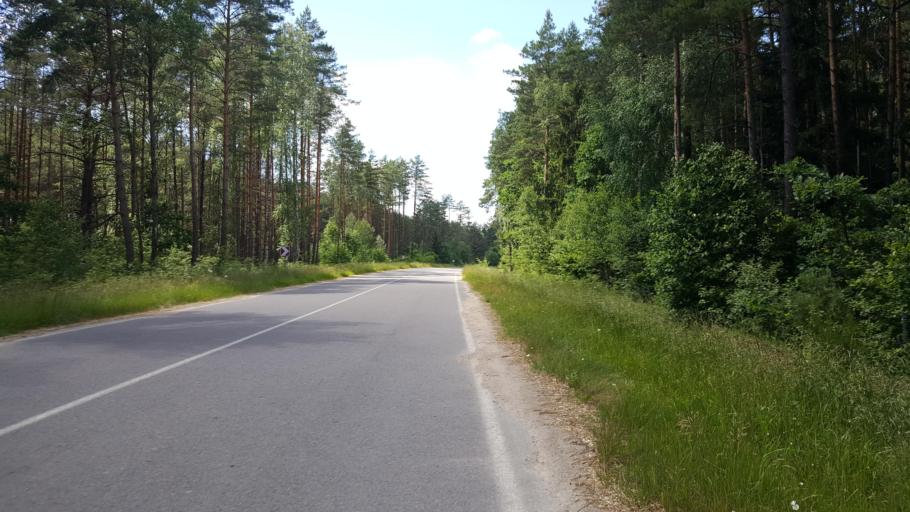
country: PL
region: Podlasie
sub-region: Powiat hajnowski
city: Czeremcha
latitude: 52.5436
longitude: 23.5037
